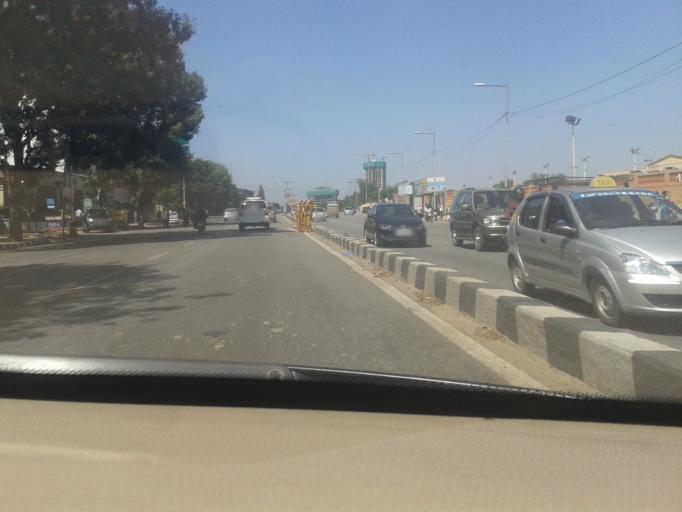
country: IN
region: Karnataka
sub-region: Bangalore Urban
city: Bangalore
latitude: 13.0096
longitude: 77.5839
